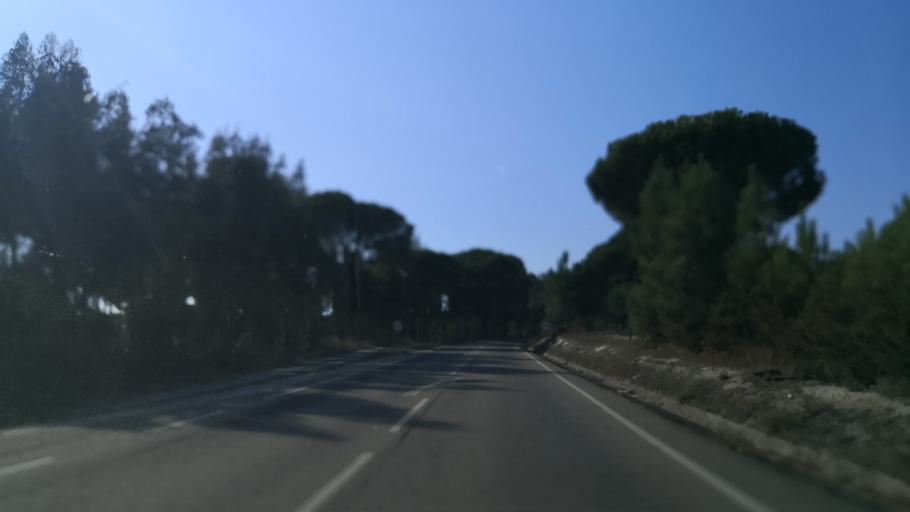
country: PT
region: Santarem
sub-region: Coruche
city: Coruche
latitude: 38.9776
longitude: -8.5428
